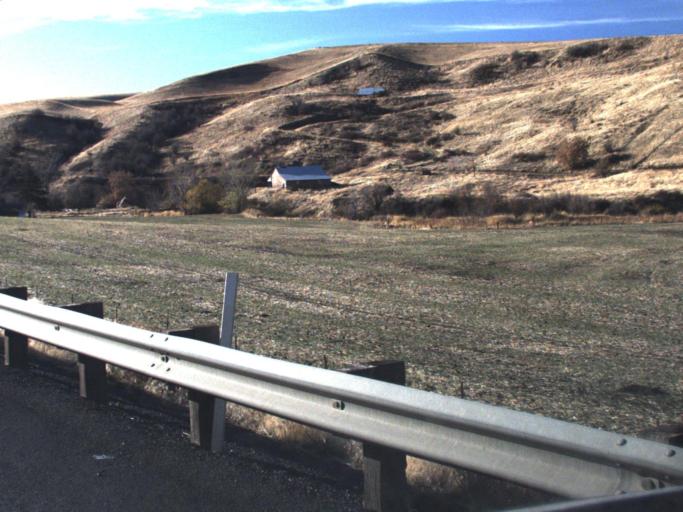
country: US
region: Washington
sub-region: Garfield County
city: Pomeroy
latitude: 46.4581
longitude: -117.4721
